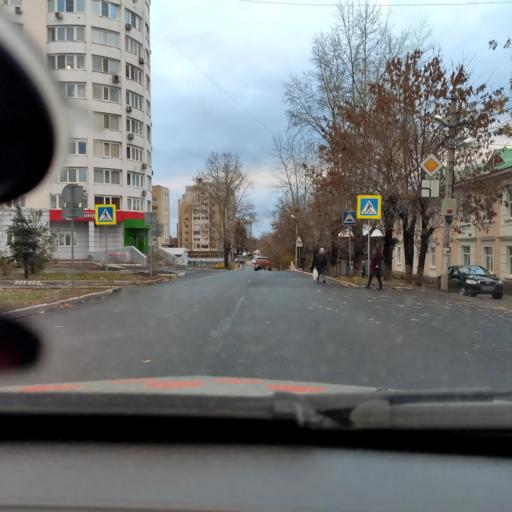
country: RU
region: Bashkortostan
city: Ufa
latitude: 54.7212
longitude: 55.9621
